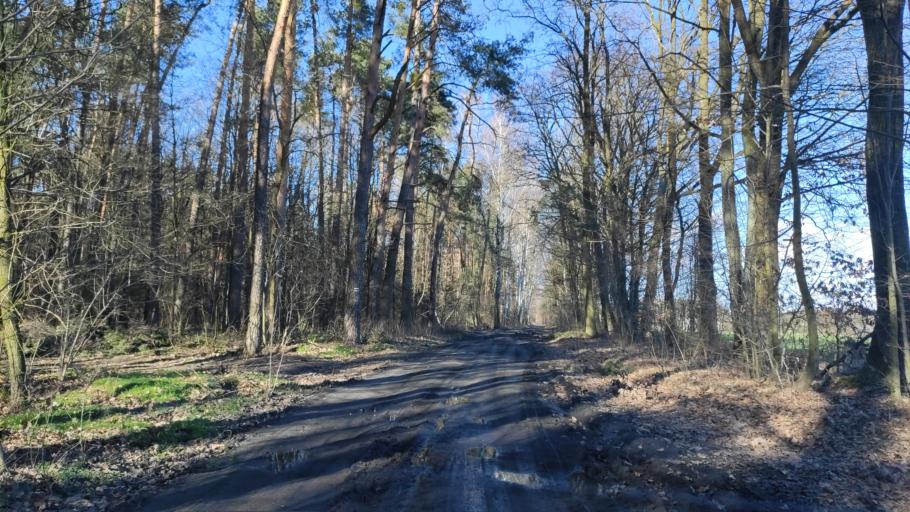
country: PL
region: Masovian Voivodeship
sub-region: Powiat radomski
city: Jedlnia-Letnisko
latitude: 51.4580
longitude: 21.3239
